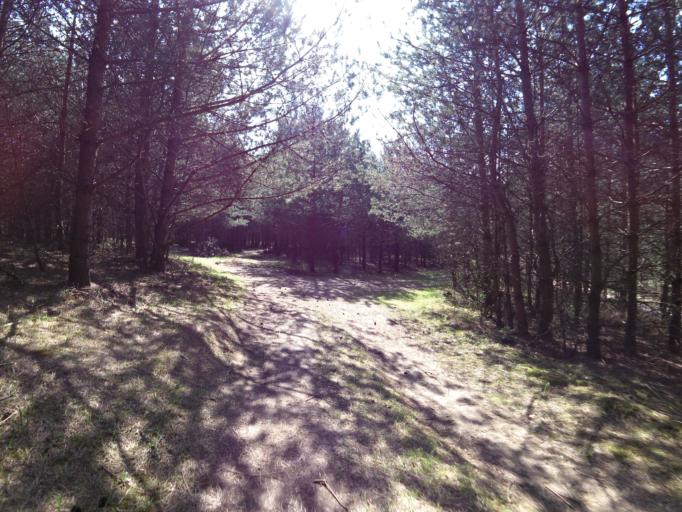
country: LT
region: Vilnius County
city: Pilaite
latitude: 54.6978
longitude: 25.2020
